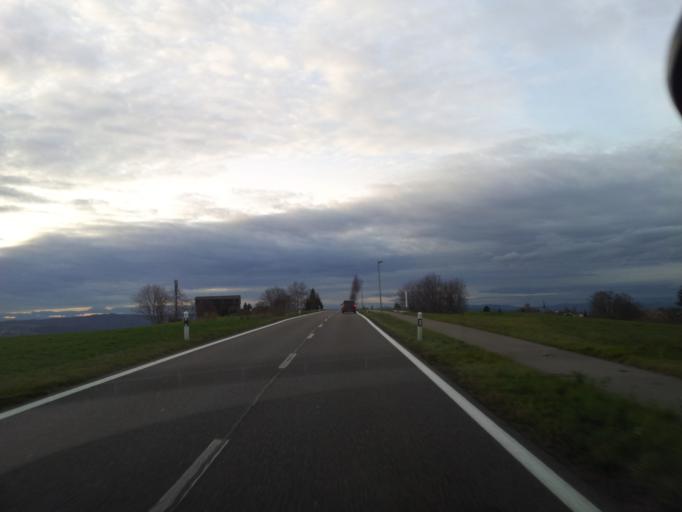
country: CH
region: Aargau
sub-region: Bezirk Bremgarten
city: Berikon
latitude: 47.3426
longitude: 8.3860
